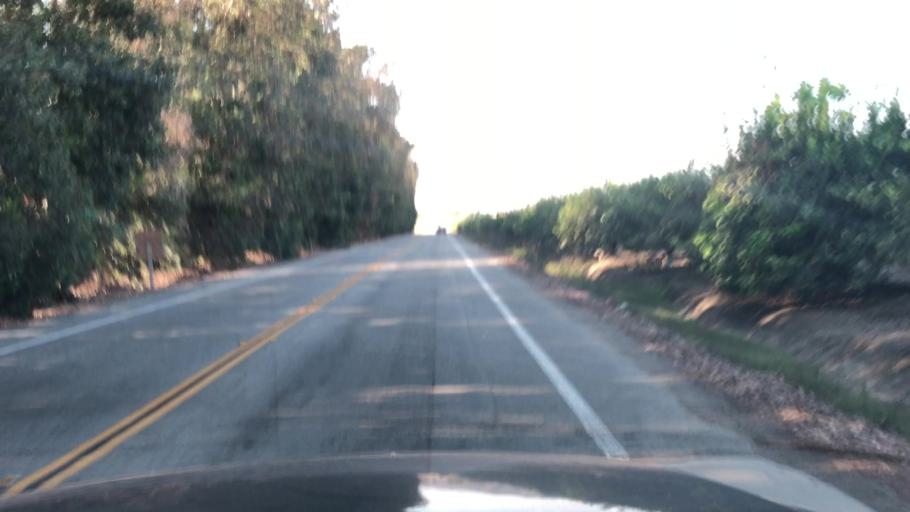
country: US
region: California
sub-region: Ventura County
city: Oxnard Shores
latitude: 34.2454
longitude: -119.2342
